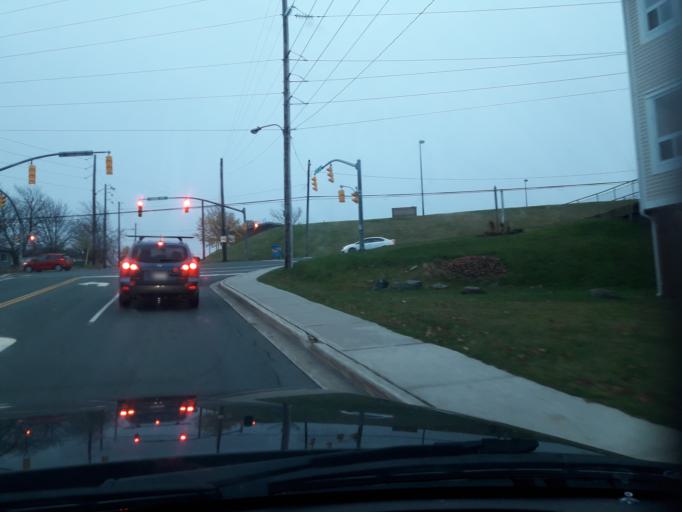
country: CA
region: Newfoundland and Labrador
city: St. John's
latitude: 47.5585
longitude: -52.7377
